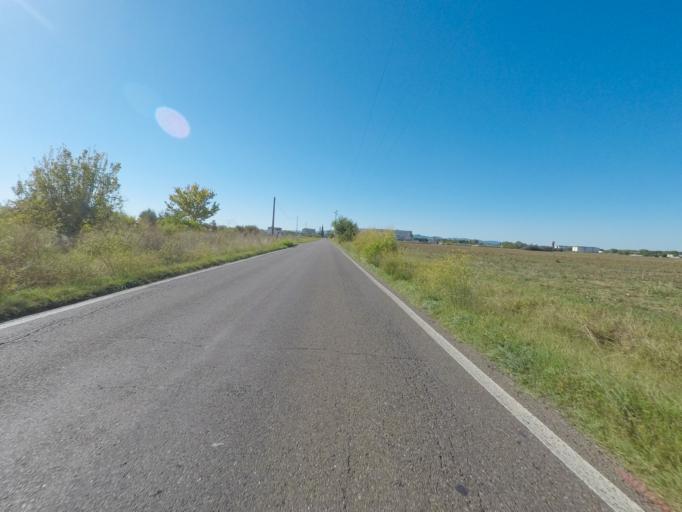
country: IT
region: Tuscany
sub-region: Provincia di Grosseto
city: Grosseto
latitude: 42.7737
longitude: 11.1365
